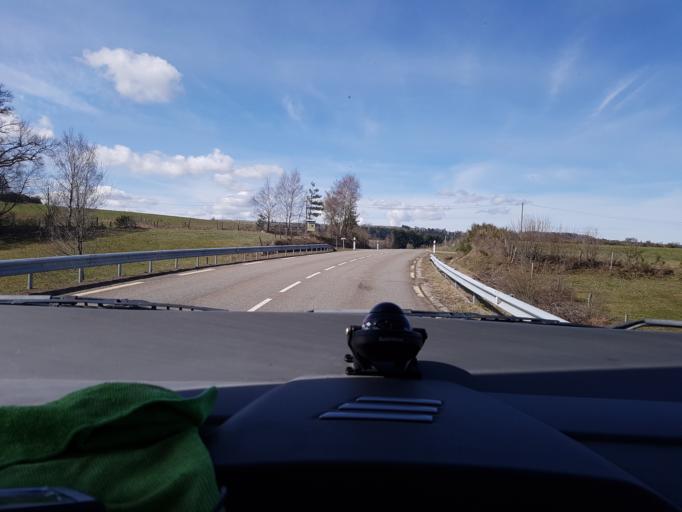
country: FR
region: Auvergne
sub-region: Departement du Cantal
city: Chaudes-Aigues
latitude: 44.7850
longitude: 2.9137
